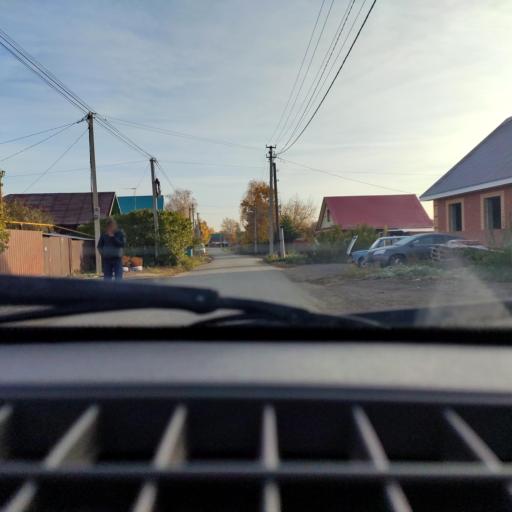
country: RU
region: Bashkortostan
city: Avdon
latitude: 54.6436
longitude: 55.7436
